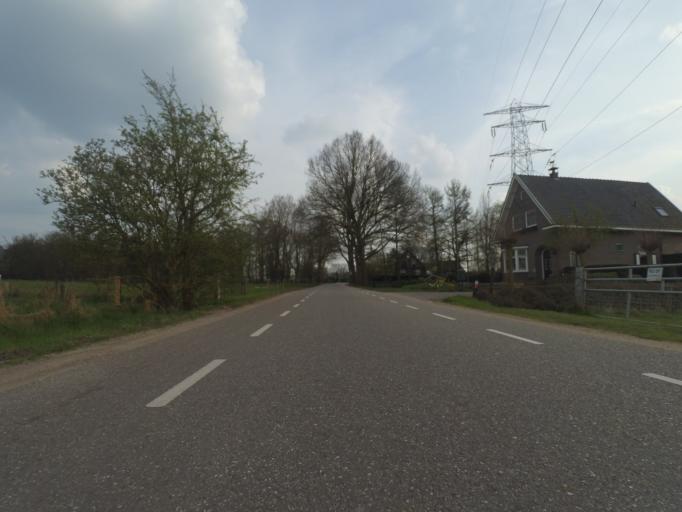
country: NL
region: Gelderland
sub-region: Gemeente Apeldoorn
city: Beekbergen
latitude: 52.1675
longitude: 5.9710
